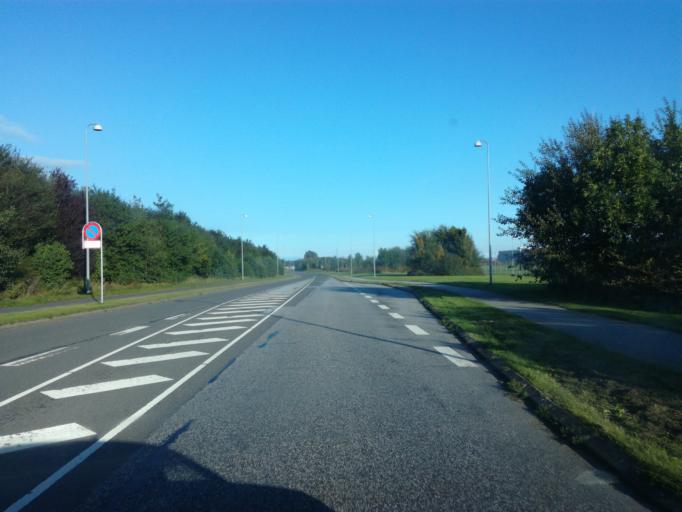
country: DK
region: South Denmark
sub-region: Fredericia Kommune
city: Taulov
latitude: 55.5525
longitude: 9.6442
